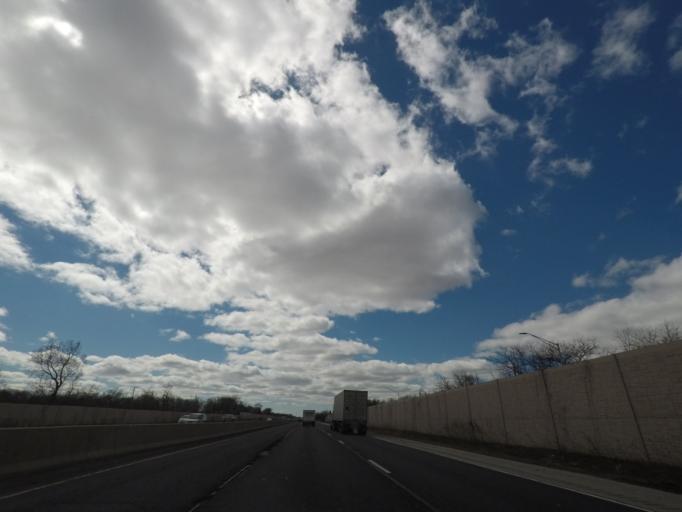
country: US
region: Illinois
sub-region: Will County
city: Crystal Lawns
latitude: 41.5636
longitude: -88.1809
